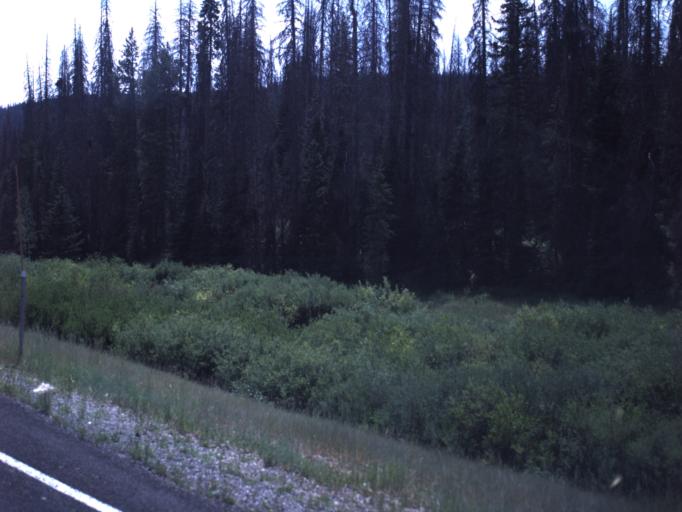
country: US
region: Utah
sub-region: Summit County
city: Francis
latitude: 40.4928
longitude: -110.9702
